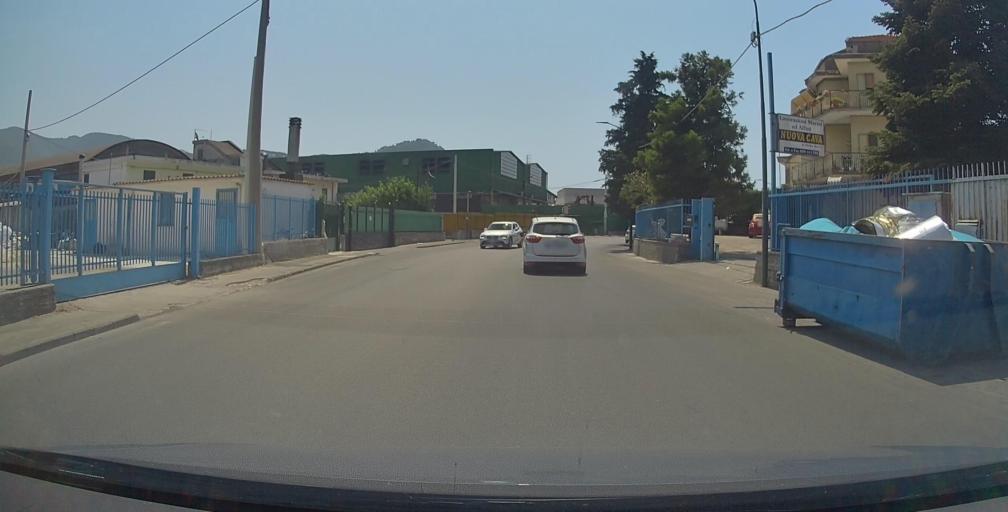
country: IT
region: Campania
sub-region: Provincia di Salerno
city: Cava De Tirreni
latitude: 40.7170
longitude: 14.6960
